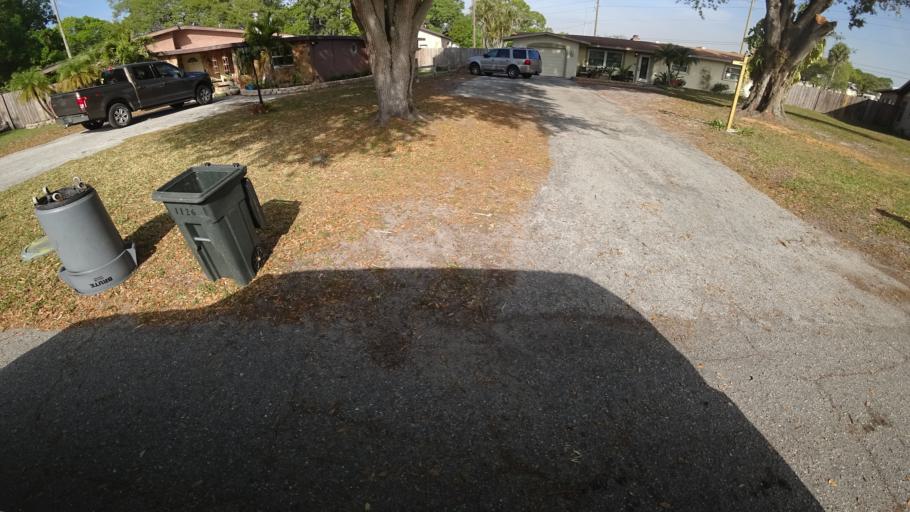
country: US
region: Florida
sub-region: Manatee County
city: Whitfield
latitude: 27.4251
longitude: -82.5523
